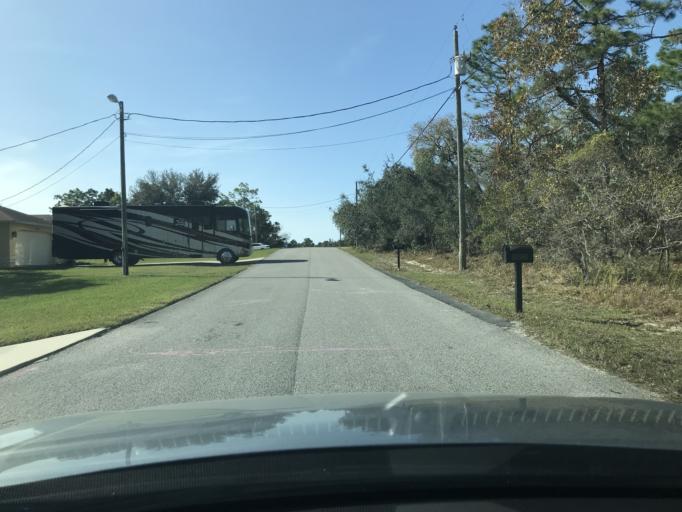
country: US
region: Florida
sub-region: Hernando County
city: North Weeki Wachee
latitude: 28.5428
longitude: -82.5485
